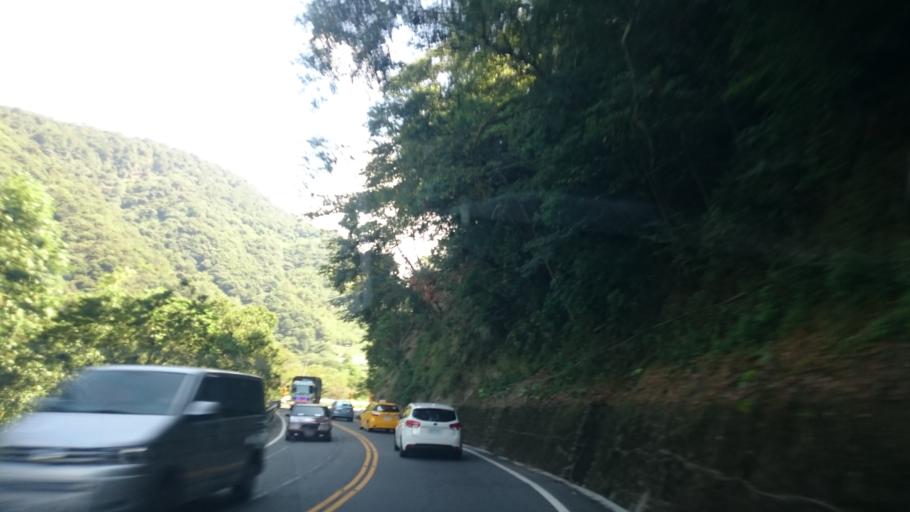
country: TW
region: Taiwan
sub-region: Nantou
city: Puli
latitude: 24.0134
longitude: 121.1198
